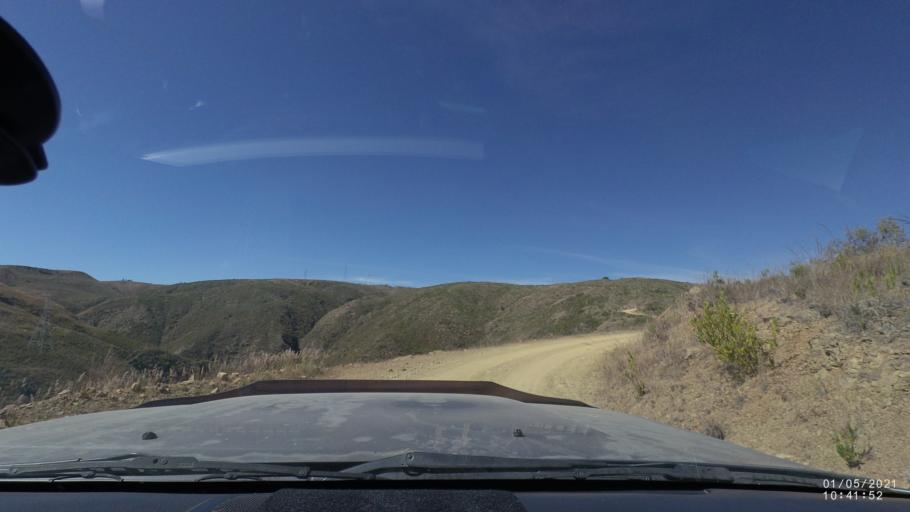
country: BO
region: Cochabamba
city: Capinota
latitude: -17.6101
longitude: -66.1759
